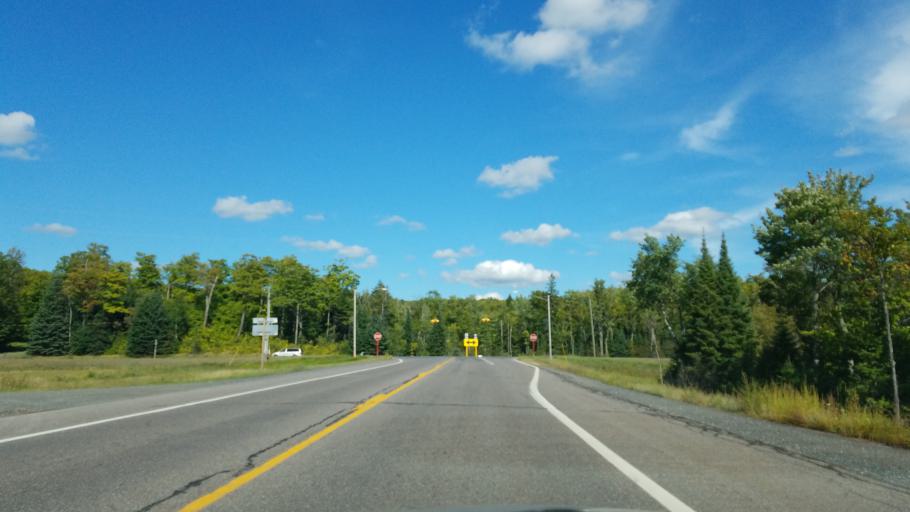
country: US
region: Michigan
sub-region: Baraga County
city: L'Anse
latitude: 46.5847
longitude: -88.4736
